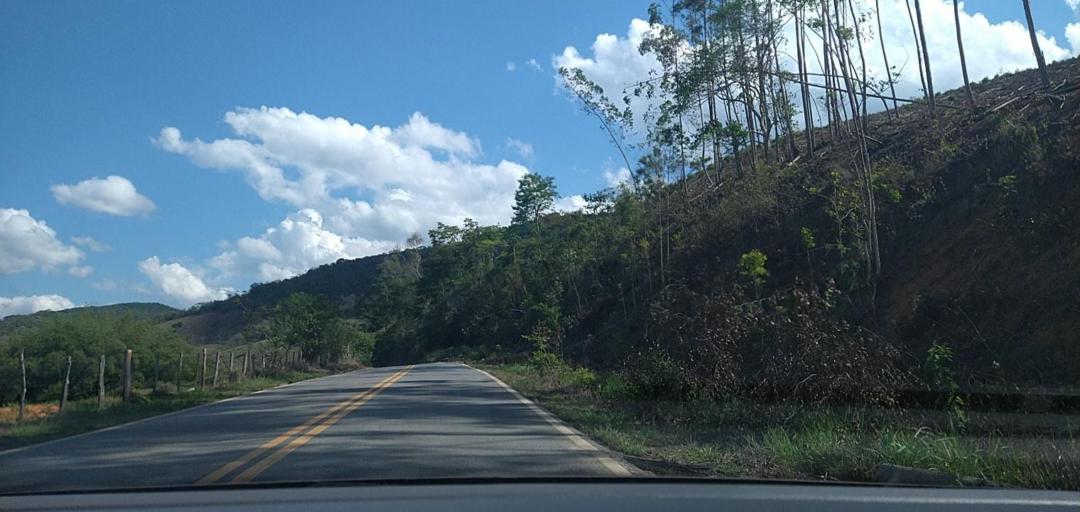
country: BR
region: Minas Gerais
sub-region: Rio Piracicaba
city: Rio Piracicaba
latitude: -19.9827
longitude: -43.1228
